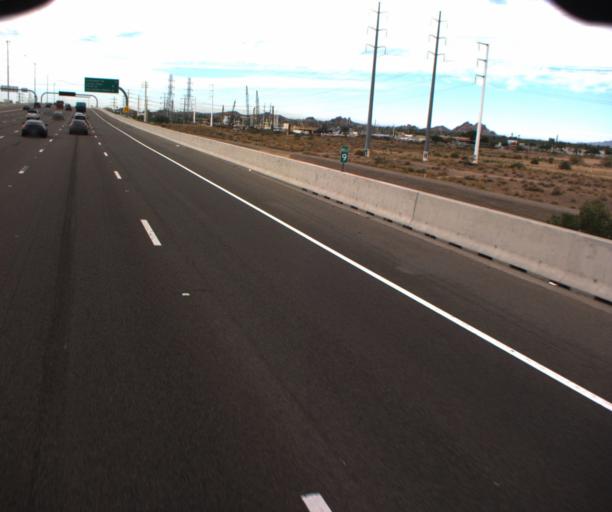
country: US
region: Arizona
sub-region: Maricopa County
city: Tempe
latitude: 33.4362
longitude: -111.9041
